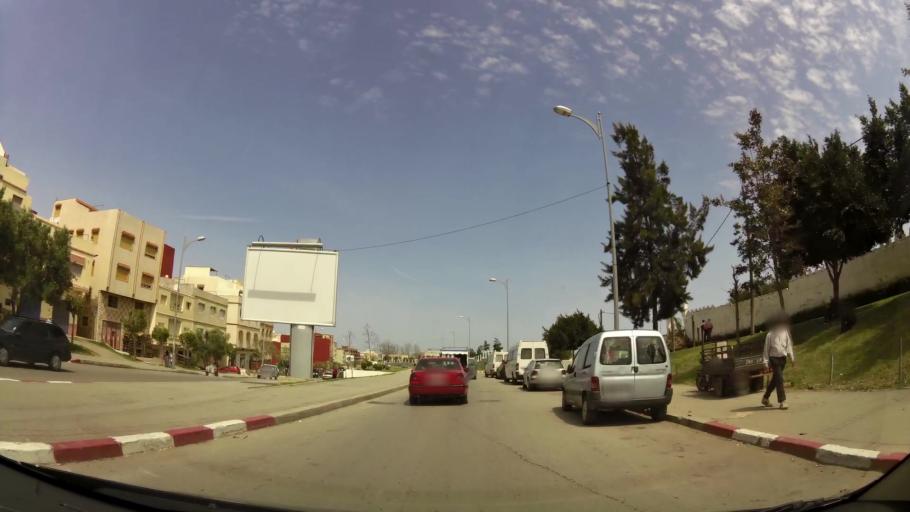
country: MA
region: Tanger-Tetouan
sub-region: Tanger-Assilah
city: Tangier
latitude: 35.7481
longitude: -5.8289
